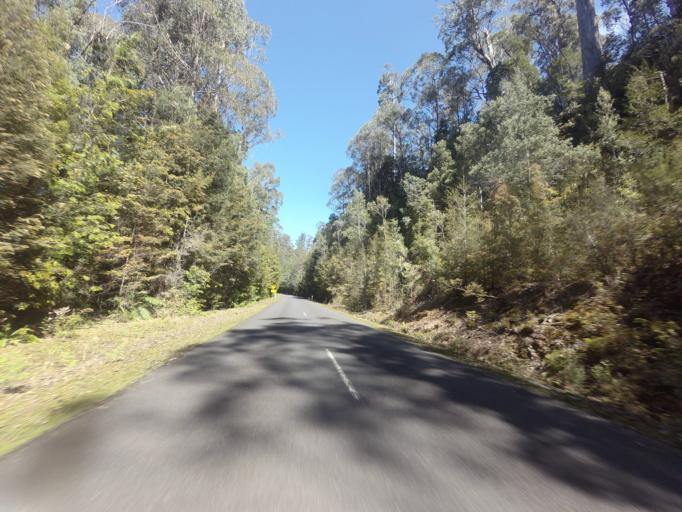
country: AU
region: Tasmania
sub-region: Huon Valley
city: Geeveston
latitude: -42.8262
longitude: 146.3164
